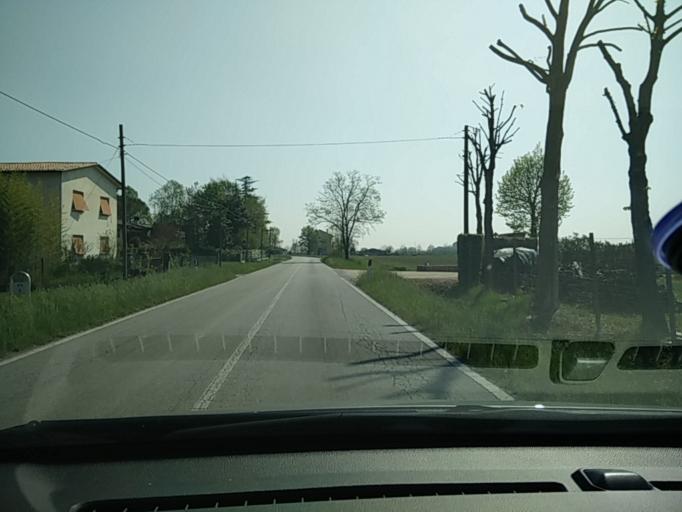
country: IT
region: Veneto
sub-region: Provincia di Treviso
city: Fornaci
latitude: 45.6690
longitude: 12.4485
